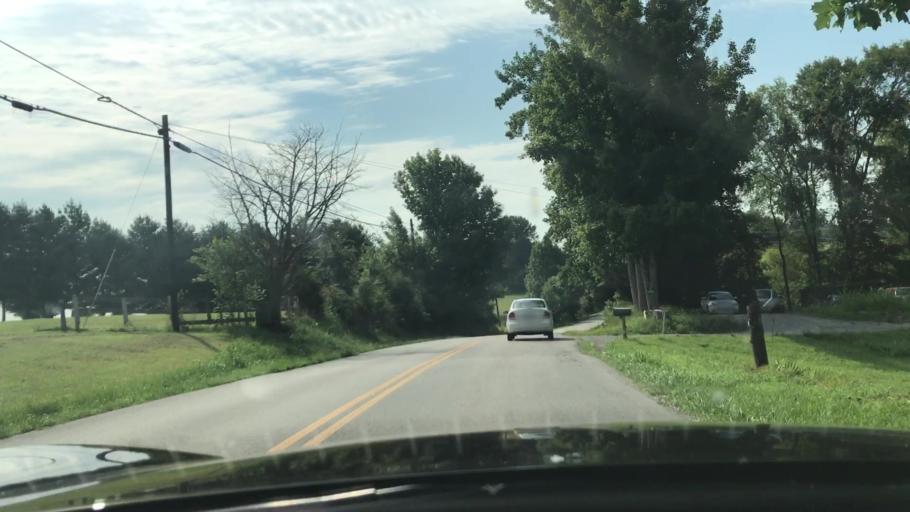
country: US
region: Kentucky
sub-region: Green County
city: Greensburg
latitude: 37.2675
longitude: -85.5642
